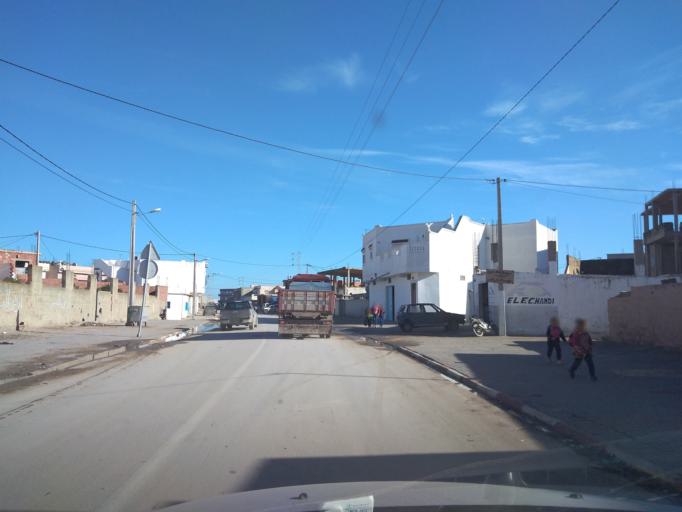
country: TN
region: Ariana
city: Qal'at al Andalus
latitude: 37.0608
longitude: 10.1257
